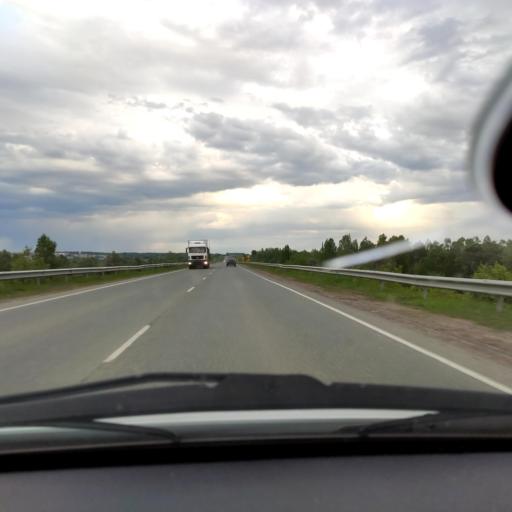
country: RU
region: Bashkortostan
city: Dyurtyuli
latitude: 55.5203
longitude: 54.8392
